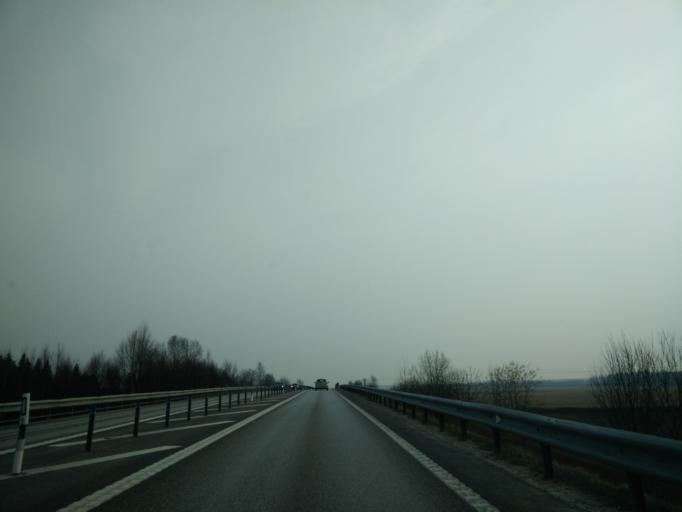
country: SE
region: Vaermland
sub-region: Forshaga Kommun
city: Forshaga
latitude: 59.4449
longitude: 13.4164
